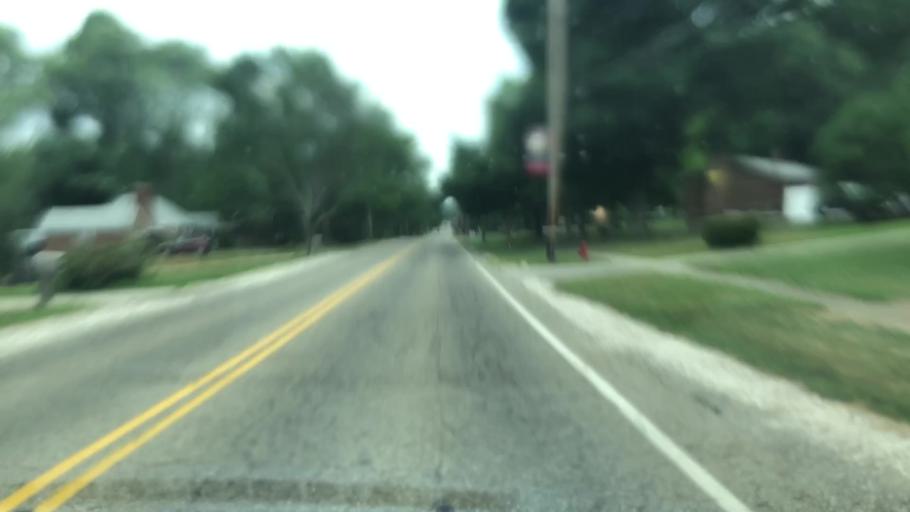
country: US
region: Ohio
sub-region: Summit County
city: Munroe Falls
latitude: 41.1402
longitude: -81.4483
